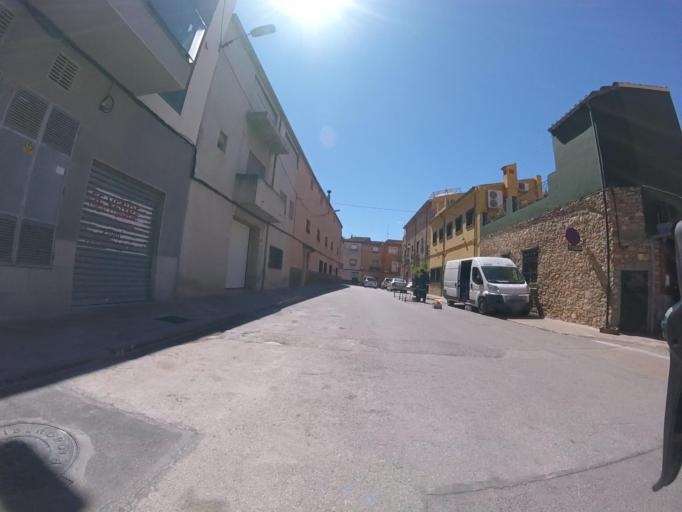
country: ES
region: Valencia
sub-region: Provincia de Castello
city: Cabanes
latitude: 40.1557
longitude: 0.0435
